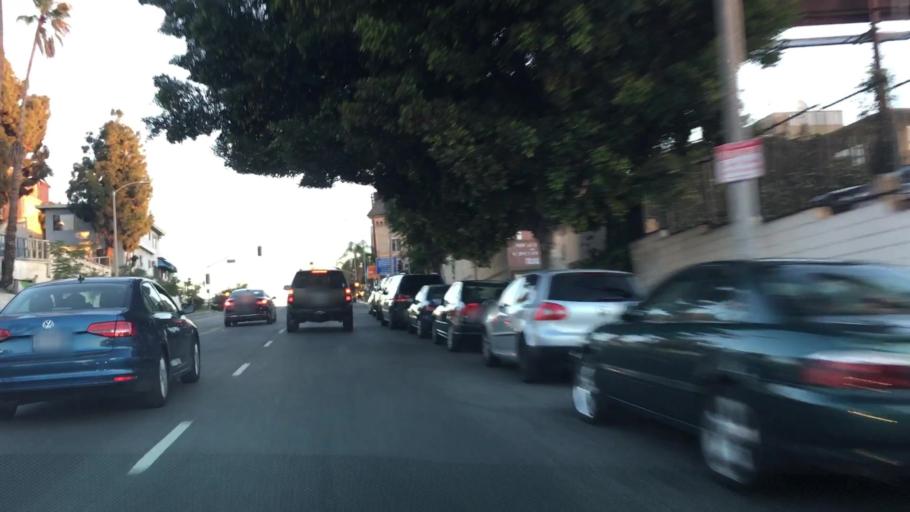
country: US
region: California
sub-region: Los Angeles County
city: Echo Park
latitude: 34.0603
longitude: -118.2667
